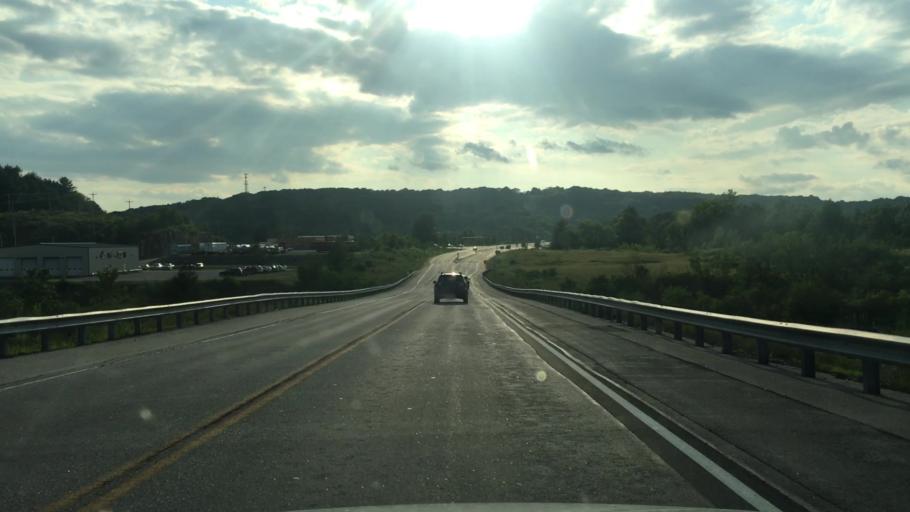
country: US
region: Maine
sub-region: Kennebec County
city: Augusta
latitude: 44.3322
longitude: -69.7546
